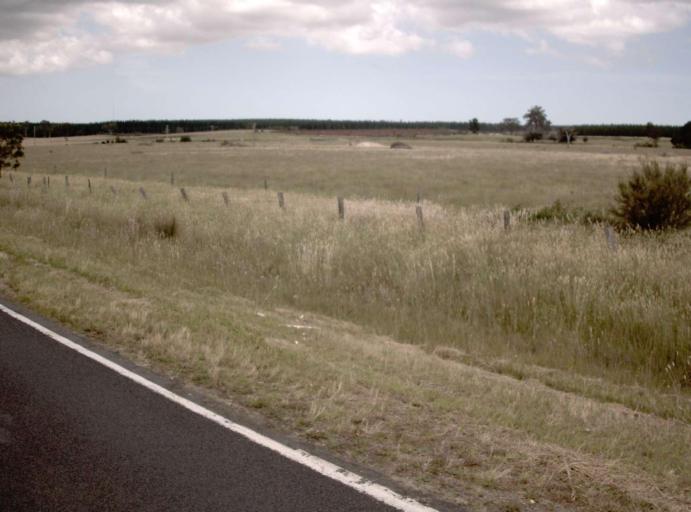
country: AU
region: Victoria
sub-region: Wellington
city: Sale
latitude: -38.1648
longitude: 147.0515
